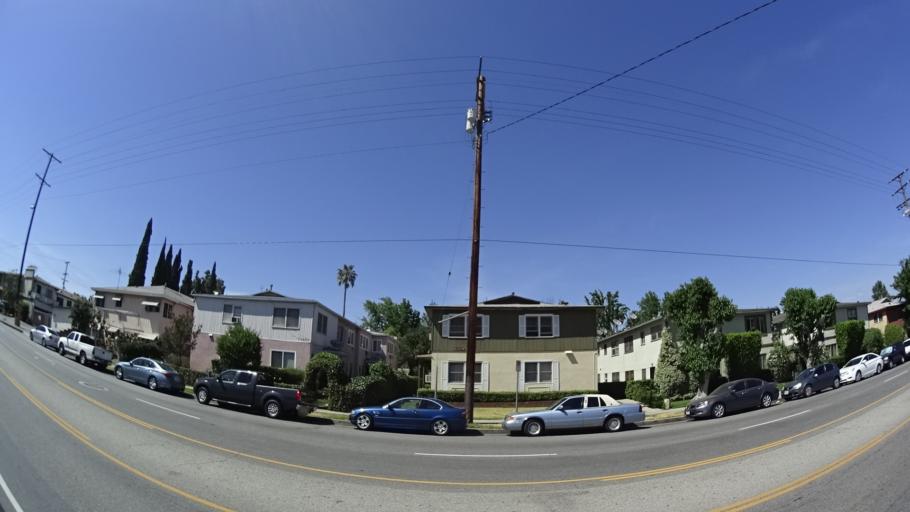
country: US
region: California
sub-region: Los Angeles County
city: Van Nuys
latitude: 34.1794
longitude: -118.4213
